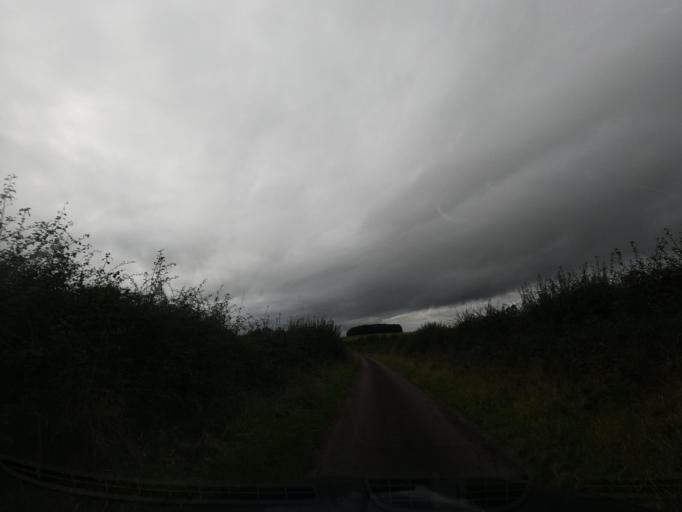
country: GB
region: England
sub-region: Northumberland
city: Ford
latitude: 55.6072
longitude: -2.0491
